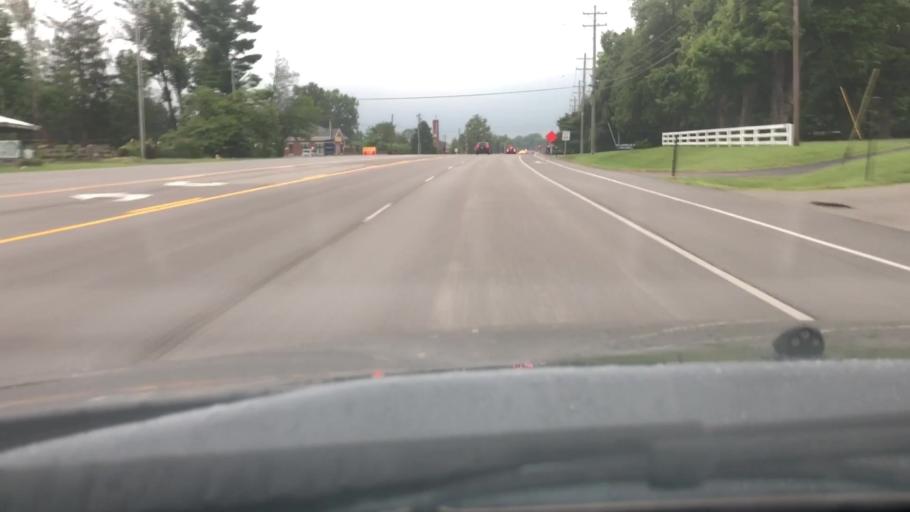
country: US
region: Kentucky
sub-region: Jefferson County
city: Hurstbourne Acres
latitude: 38.2085
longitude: -85.5840
